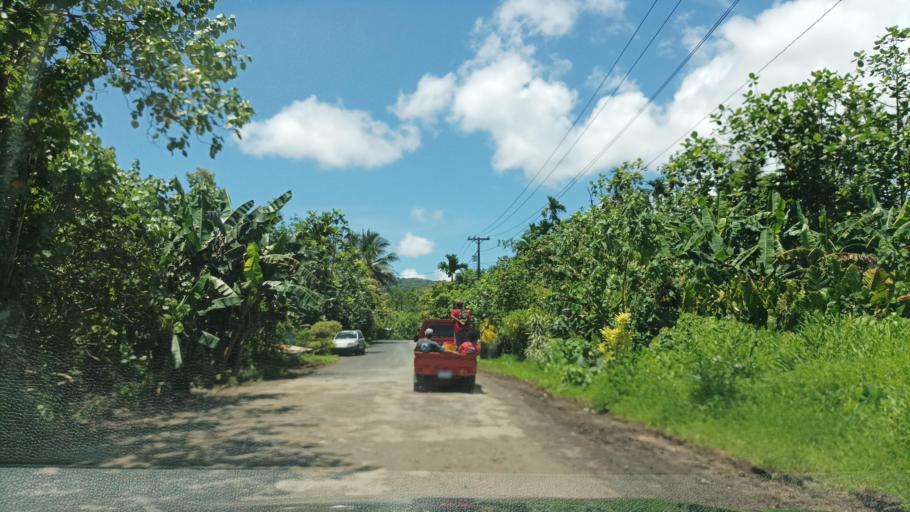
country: FM
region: Pohnpei
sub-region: Kolonia Municipality
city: Kolonia
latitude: 6.9311
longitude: 158.2781
